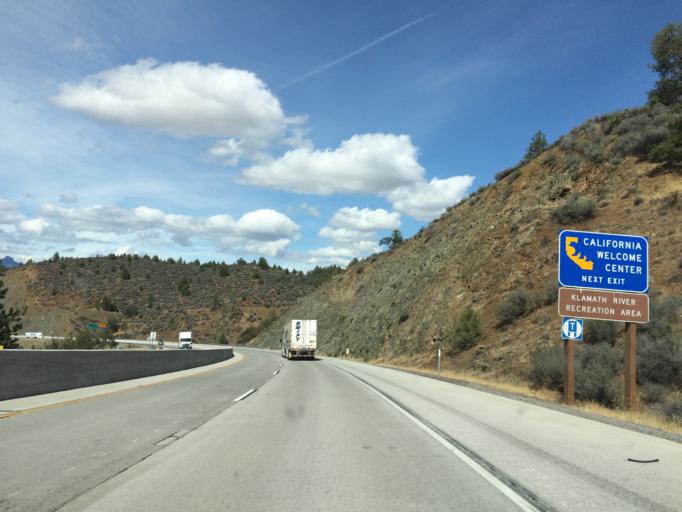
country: US
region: California
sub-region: Siskiyou County
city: Montague
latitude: 41.8460
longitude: -122.5692
